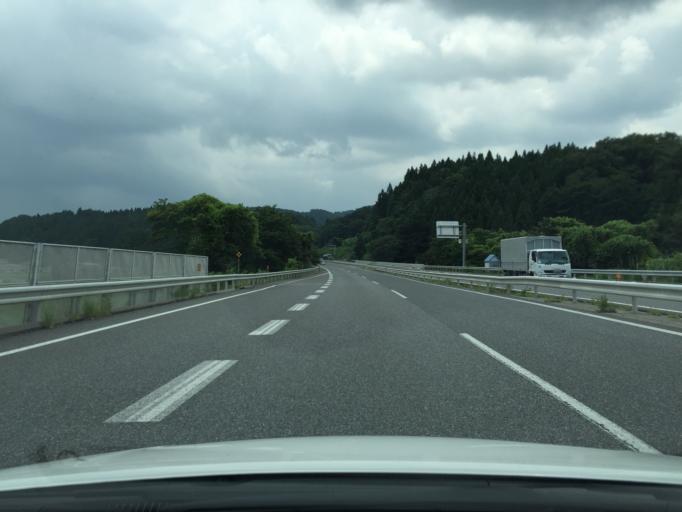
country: JP
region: Fukushima
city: Funehikimachi-funehiki
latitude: 37.2880
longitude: 140.6130
